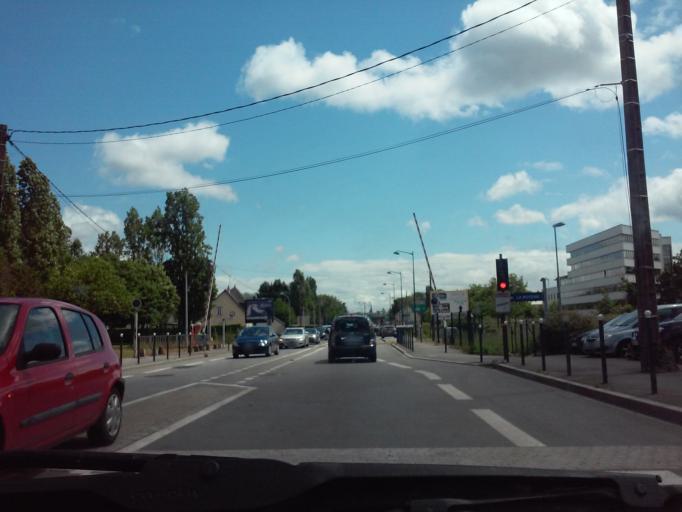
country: FR
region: Brittany
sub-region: Departement d'Ille-et-Vilaine
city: Chantepie
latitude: 48.0932
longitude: -1.6316
